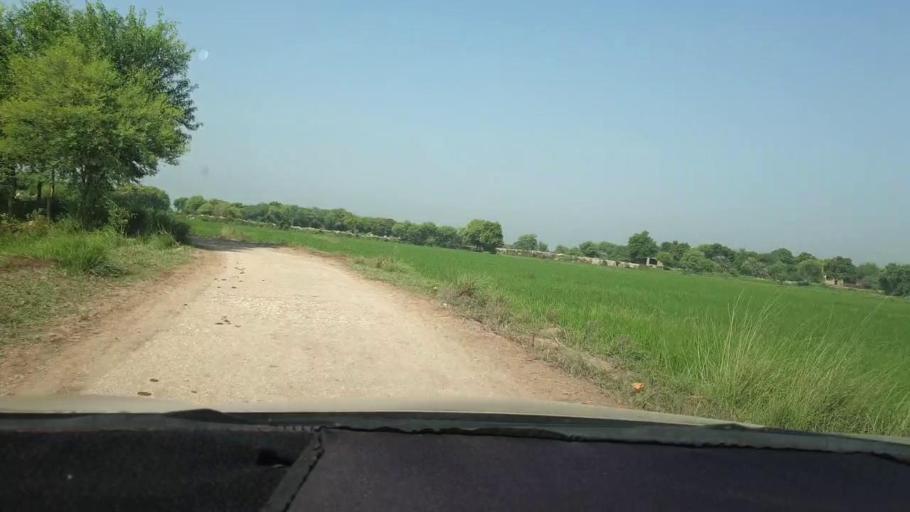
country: PK
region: Sindh
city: Miro Khan
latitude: 27.7040
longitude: 68.0896
